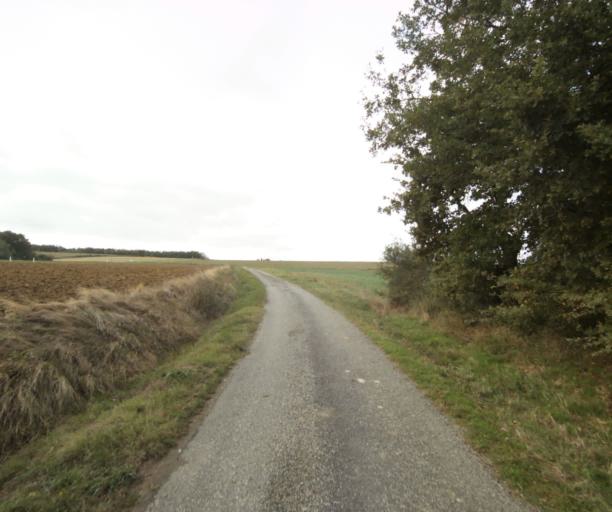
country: FR
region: Midi-Pyrenees
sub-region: Departement du Tarn-et-Garonne
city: Beaumont-de-Lomagne
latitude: 43.8676
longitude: 1.0918
